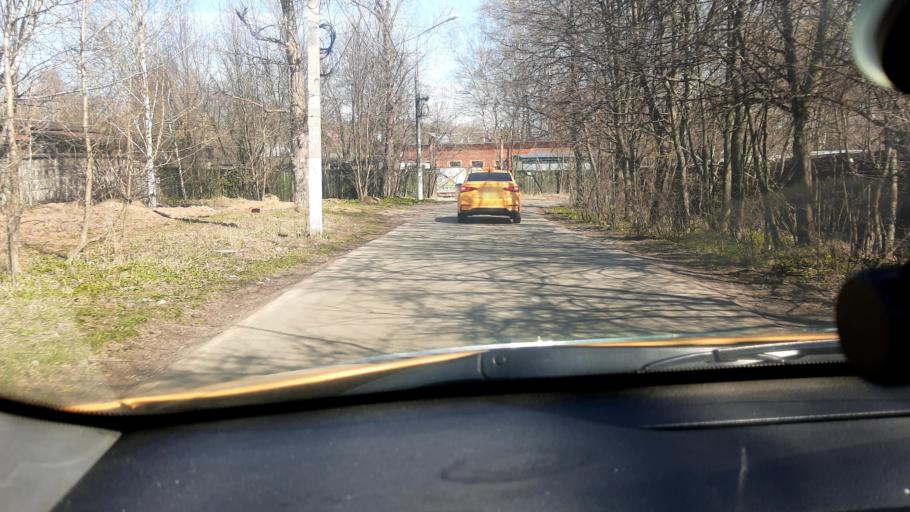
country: RU
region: Moscow
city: Annino
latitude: 55.5323
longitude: 37.6004
